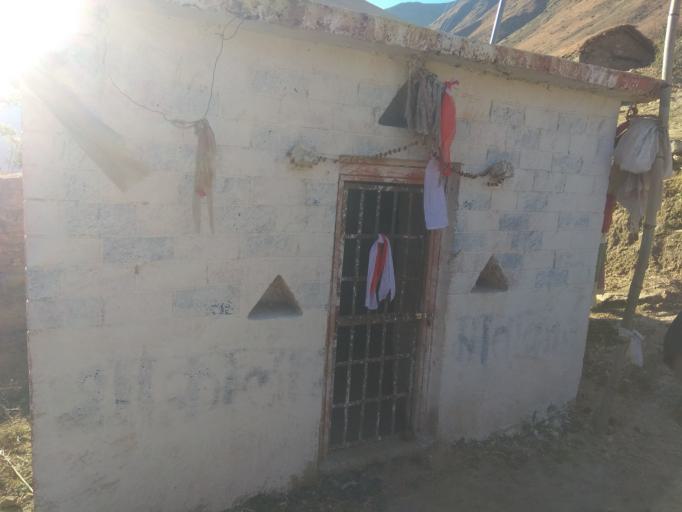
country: NP
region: Mid Western
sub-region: Bheri Zone
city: Dailekh
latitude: 29.2597
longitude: 81.6793
